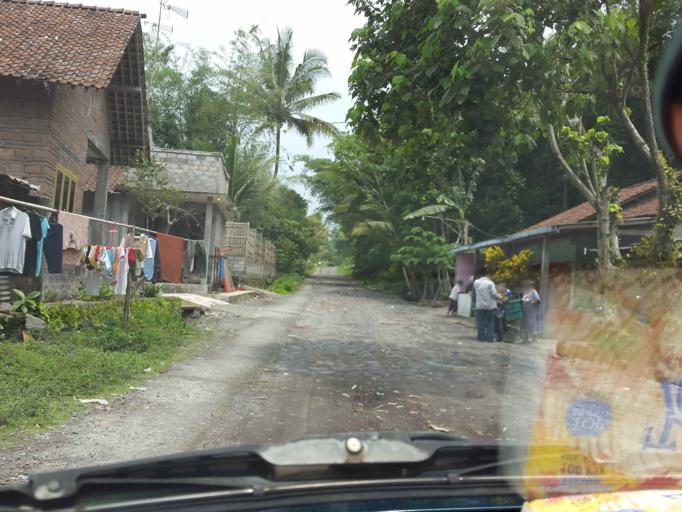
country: ID
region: Central Java
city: Muntilan
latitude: -7.6000
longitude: 110.3084
